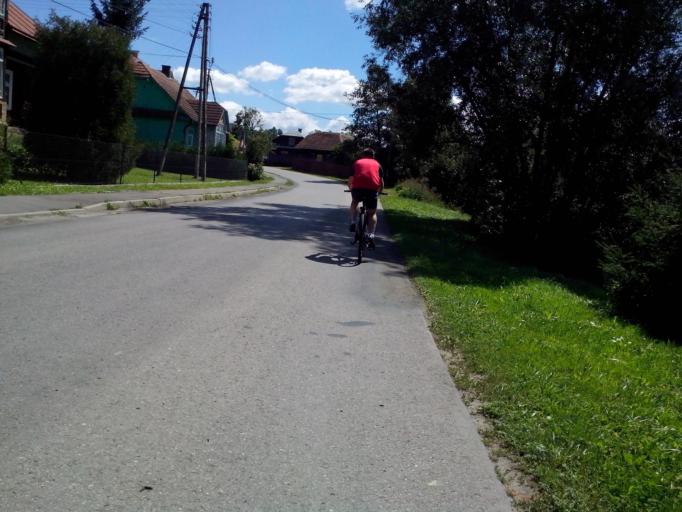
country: PL
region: Subcarpathian Voivodeship
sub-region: Powiat brzozowski
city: Blizne
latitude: 49.7882
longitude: 21.9835
